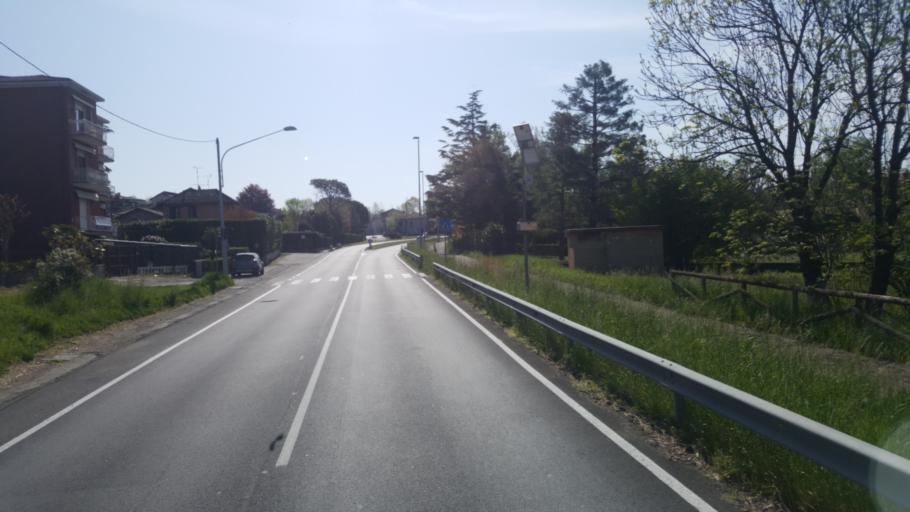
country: IT
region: Lombardy
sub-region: Provincia di Varese
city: Gavirate
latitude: 45.8393
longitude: 8.7278
